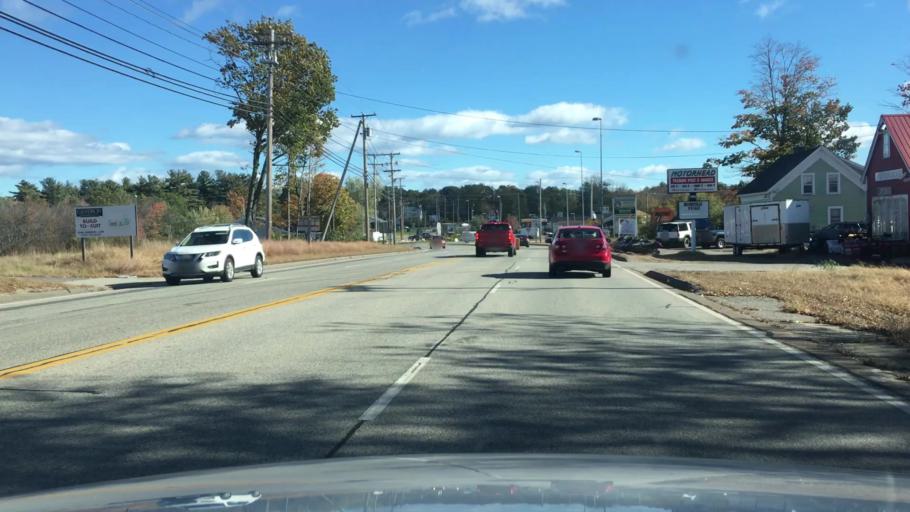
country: US
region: Maine
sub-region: York County
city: South Sanford
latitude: 43.4121
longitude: -70.7443
